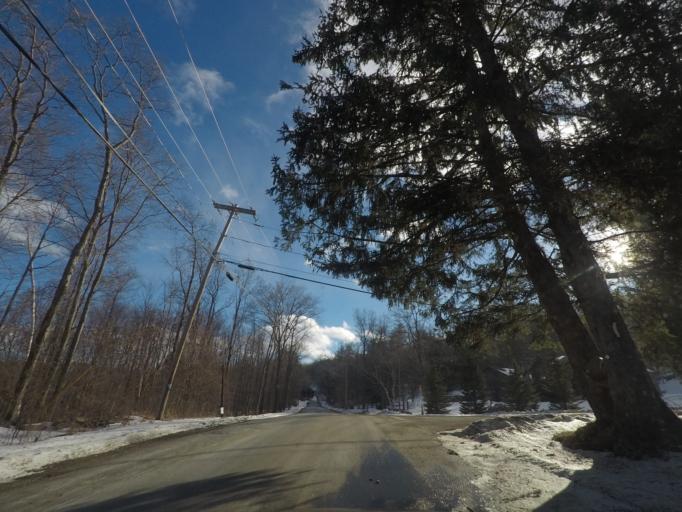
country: US
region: New York
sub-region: Rensselaer County
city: Hoosick Falls
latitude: 42.8201
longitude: -73.3906
